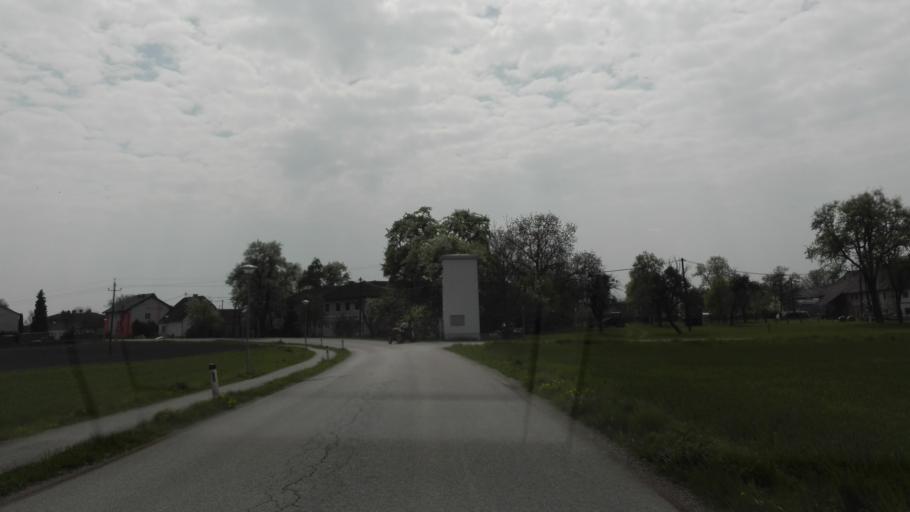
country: AT
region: Upper Austria
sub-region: Politischer Bezirk Perg
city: Perg
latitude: 48.2299
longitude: 14.6009
